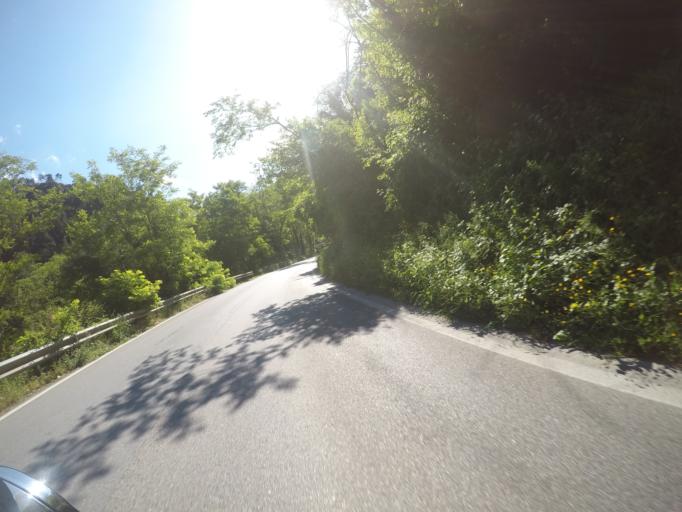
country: IT
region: Tuscany
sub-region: Provincia di Massa-Carrara
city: Montignoso
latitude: 44.0460
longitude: 10.1503
